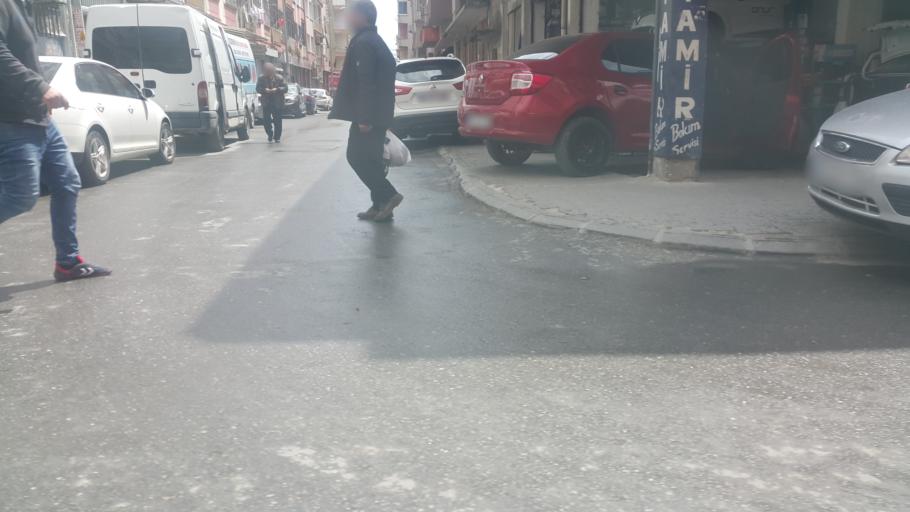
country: TR
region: Mersin
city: Mercin
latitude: 36.8056
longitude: 34.6249
